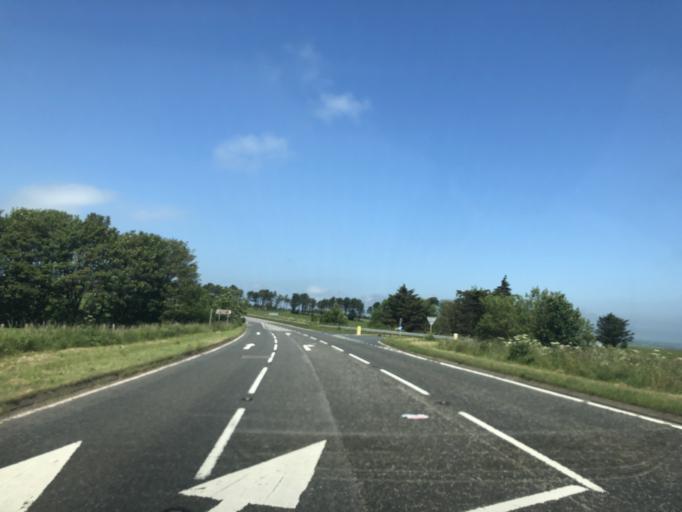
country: GB
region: Scotland
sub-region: Aberdeenshire
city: Stonehaven
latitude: 56.9414
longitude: -2.2075
